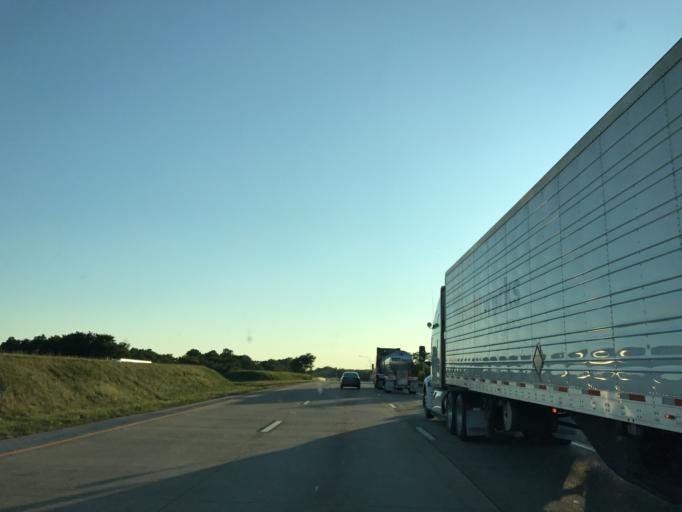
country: US
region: Delaware
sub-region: New Castle County
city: Wilmington
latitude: 39.7172
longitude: -75.5574
